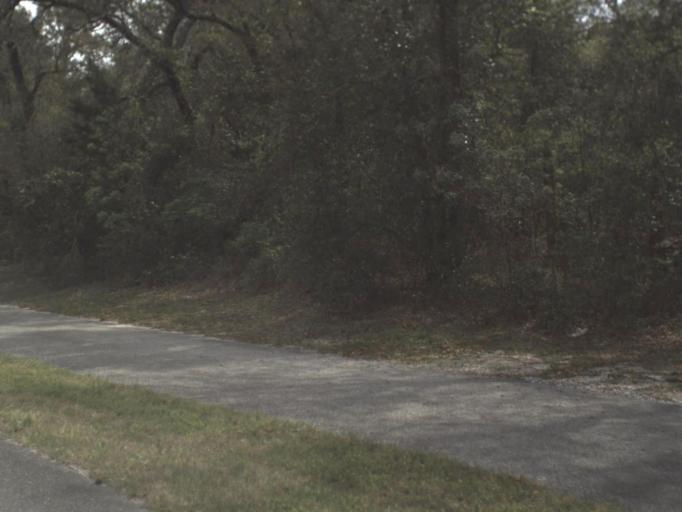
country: US
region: Florida
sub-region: Santa Rosa County
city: Gulf Breeze
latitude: 30.3633
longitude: -87.1382
